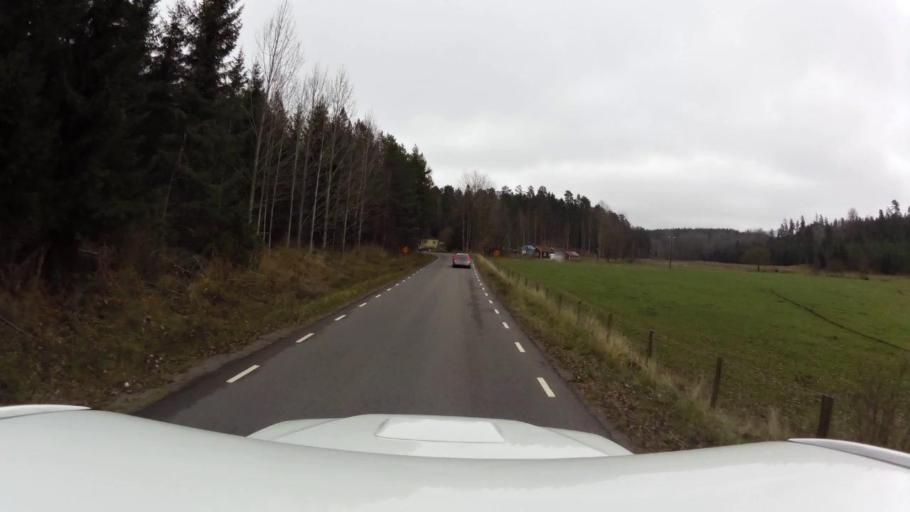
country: SE
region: OEstergoetland
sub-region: Kinda Kommun
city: Kisa
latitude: 58.1170
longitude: 15.4227
